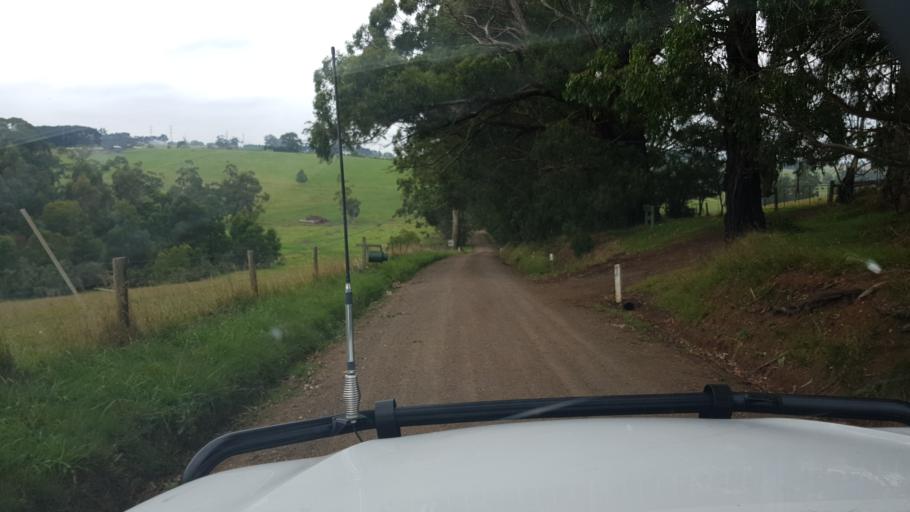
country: AU
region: Victoria
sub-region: Baw Baw
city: Warragul
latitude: -38.1247
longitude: 145.9970
